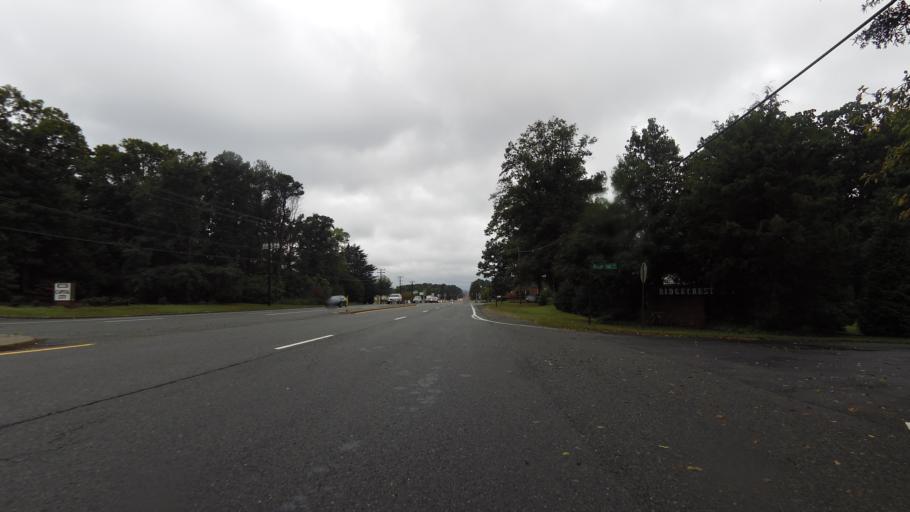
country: US
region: Virginia
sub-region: Henrico County
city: Tuckahoe
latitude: 37.5950
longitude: -77.5710
